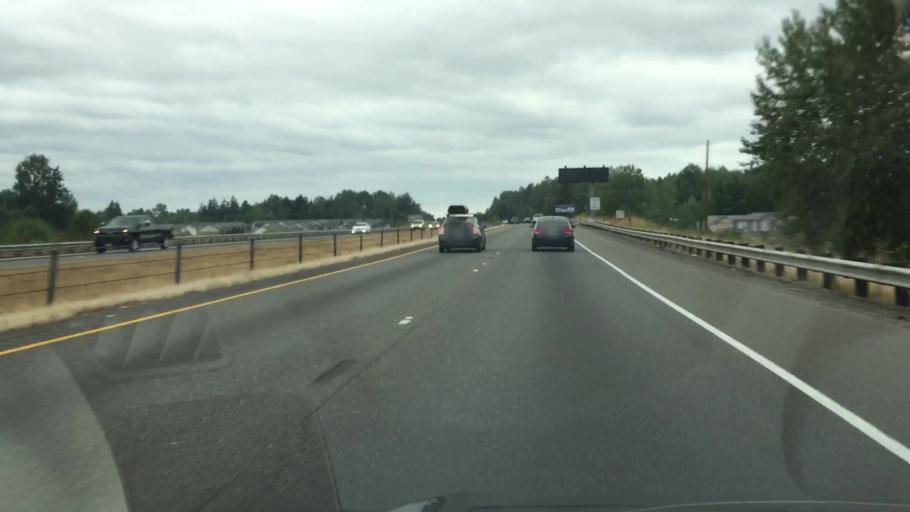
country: US
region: Washington
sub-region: Pierce County
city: Midland
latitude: 47.1592
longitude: -122.4113
